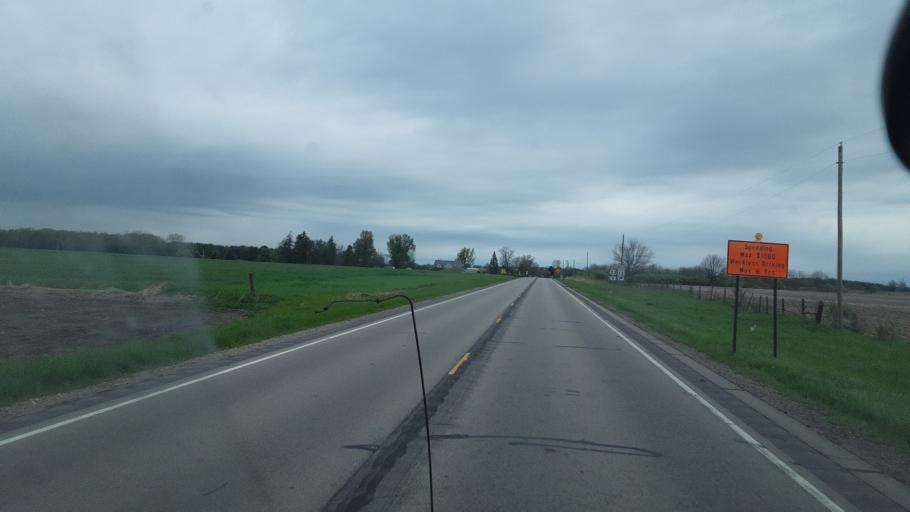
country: US
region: Indiana
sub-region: Kosciusko County
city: Syracuse
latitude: 41.4623
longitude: -85.6975
